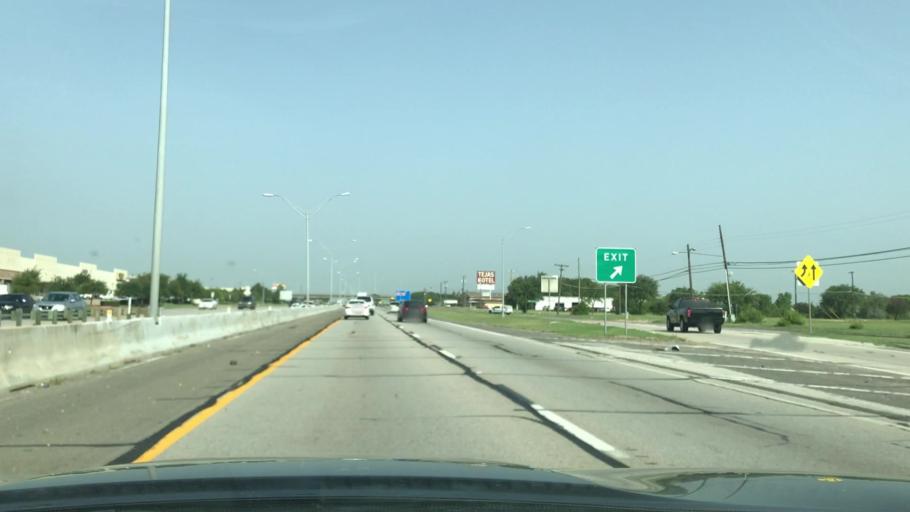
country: US
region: Texas
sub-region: Dallas County
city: Mesquite
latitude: 32.7956
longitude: -96.6625
